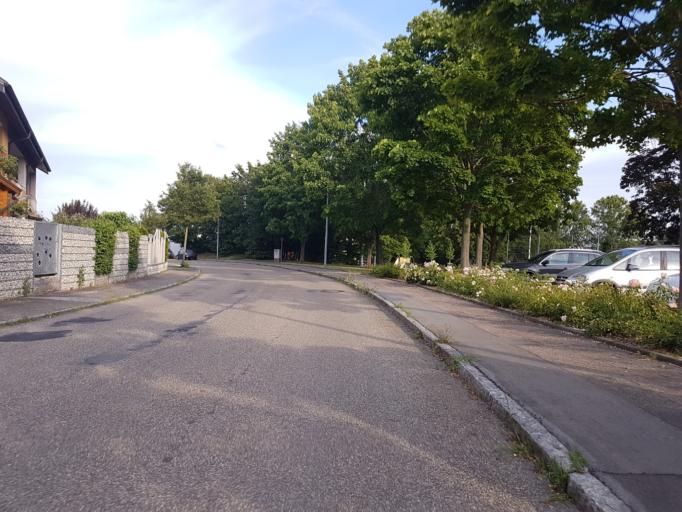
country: DE
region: Baden-Wuerttemberg
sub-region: Regierungsbezirk Stuttgart
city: Brackenheim
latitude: 49.0682
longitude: 9.0906
